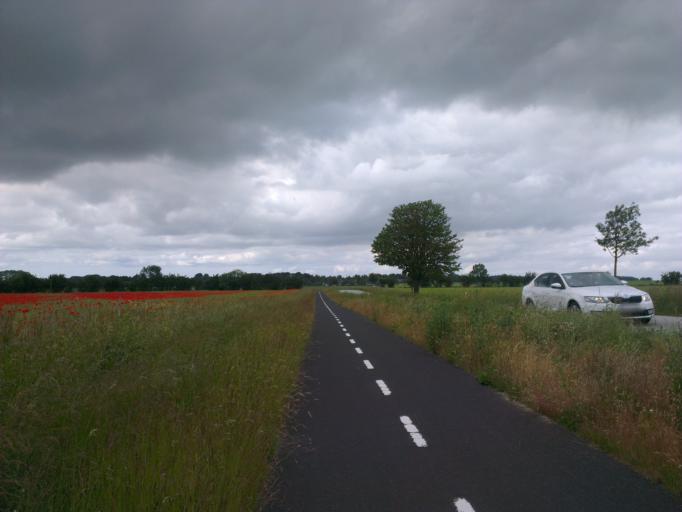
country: DK
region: Capital Region
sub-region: Frederikssund Kommune
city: Skibby
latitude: 55.6936
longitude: 11.9492
